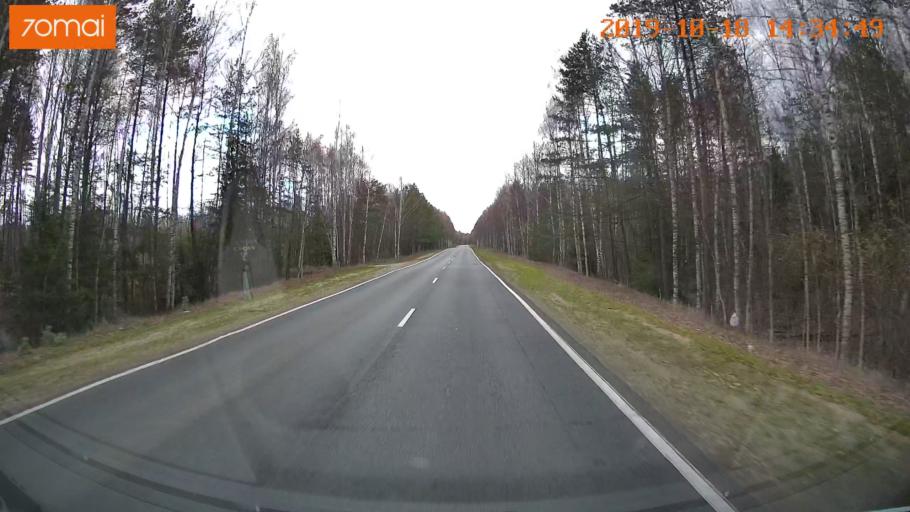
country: RU
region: Vladimir
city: Velikodvorskiy
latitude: 55.2165
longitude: 40.6240
